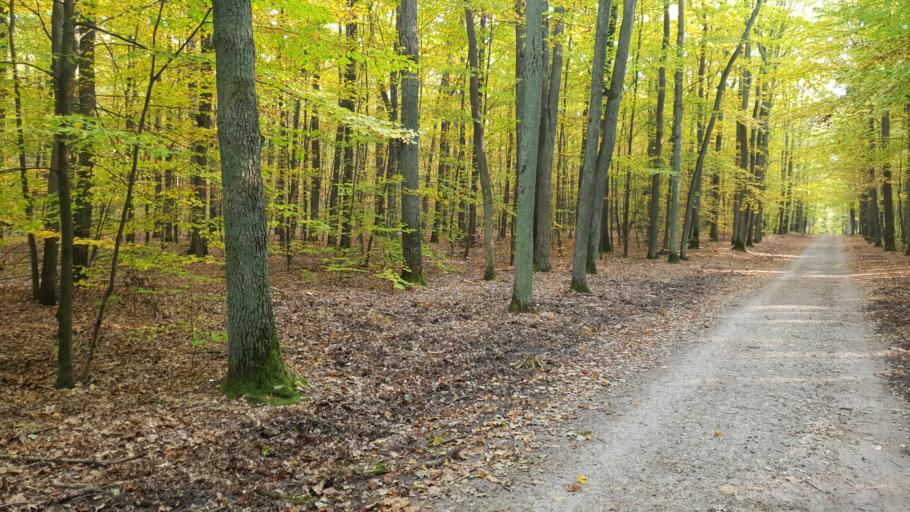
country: PL
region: Lodz Voivodeship
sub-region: Powiat zgierski
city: Zgierz
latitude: 51.8343
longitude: 19.4703
